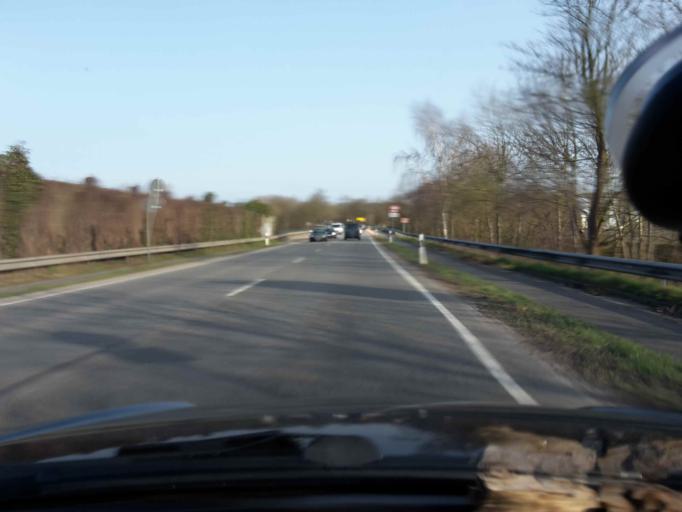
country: DE
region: Lower Saxony
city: Buxtehude
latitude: 53.4624
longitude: 9.6905
